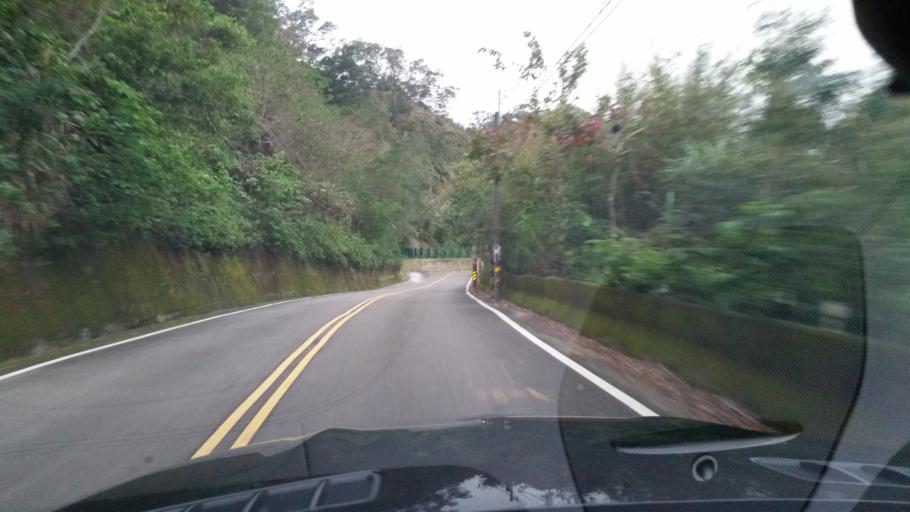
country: TW
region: Taiwan
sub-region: Miaoli
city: Miaoli
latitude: 24.5803
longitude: 120.8863
